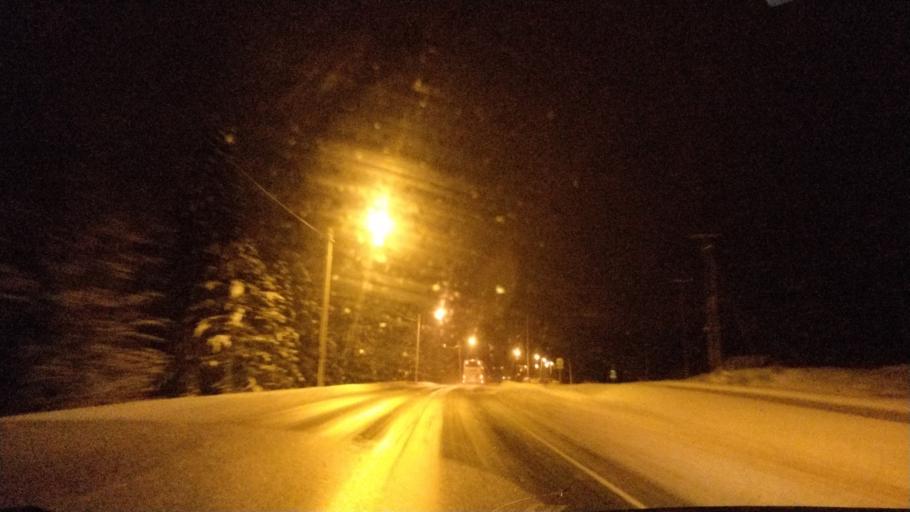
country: FI
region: Lapland
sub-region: Rovaniemi
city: Rovaniemi
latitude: 66.2891
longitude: 25.3479
